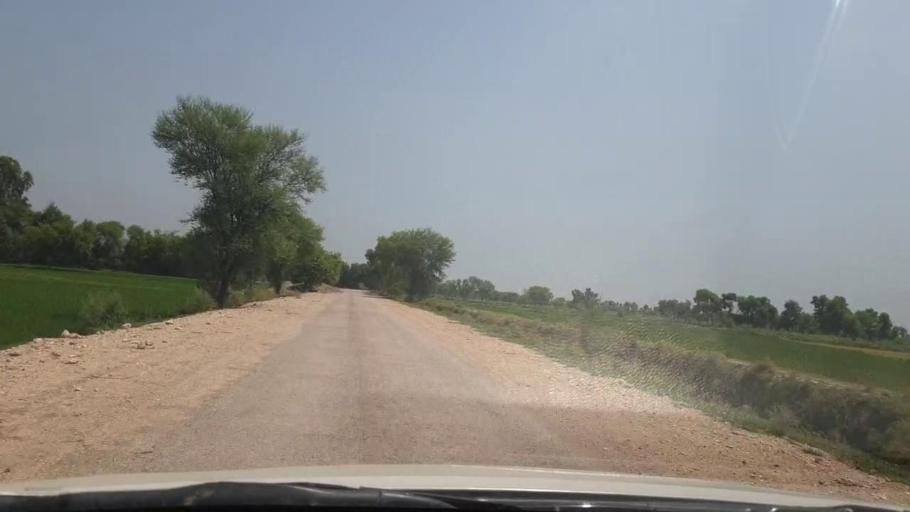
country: PK
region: Sindh
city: Rustam jo Goth
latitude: 28.0285
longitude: 68.7593
